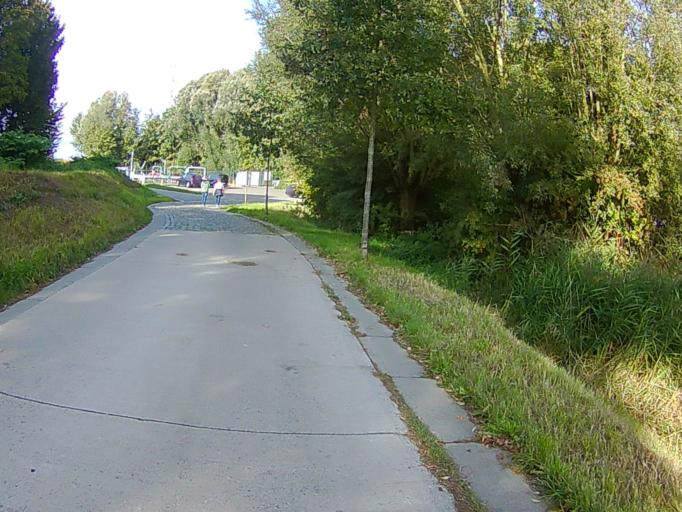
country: BE
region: Flanders
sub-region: Provincie Oost-Vlaanderen
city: Kruibeke
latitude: 51.1342
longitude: 4.2989
